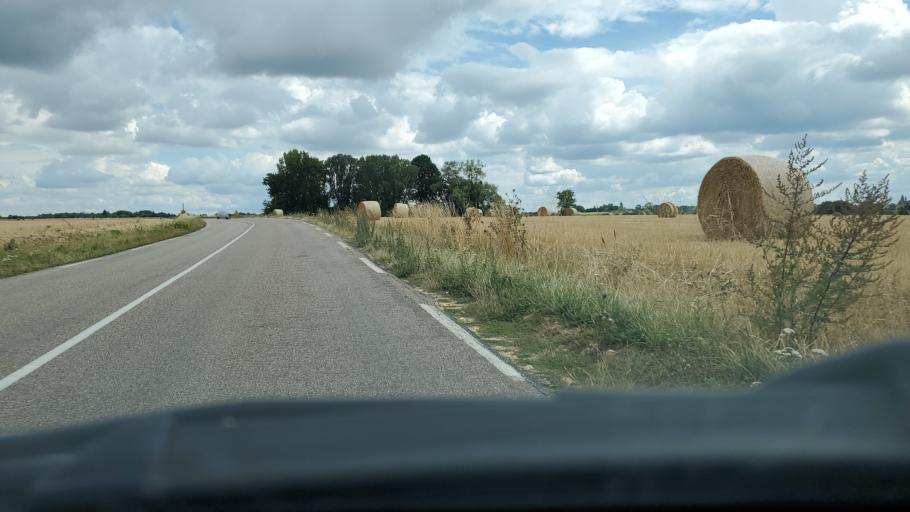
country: FR
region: Ile-de-France
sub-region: Departement de Seine-et-Marne
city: Fublaines
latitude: 48.9084
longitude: 2.9261
